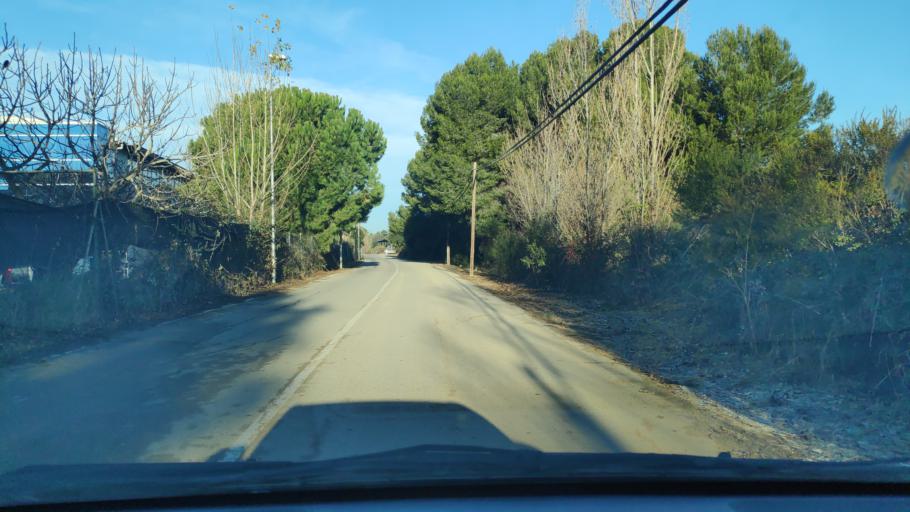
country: ES
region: Catalonia
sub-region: Provincia de Barcelona
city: Barbera del Valles
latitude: 41.5018
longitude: 2.1134
